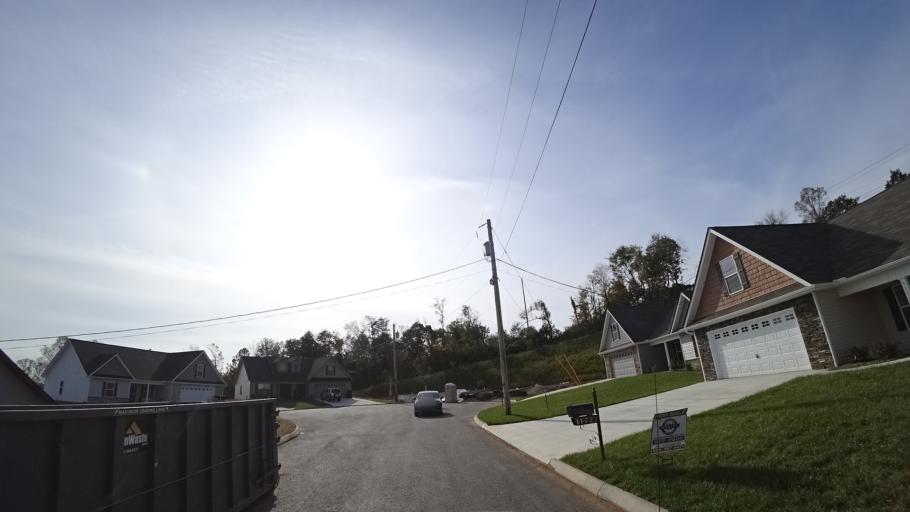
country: US
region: Tennessee
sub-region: Knox County
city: Farragut
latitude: 35.9095
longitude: -84.1768
